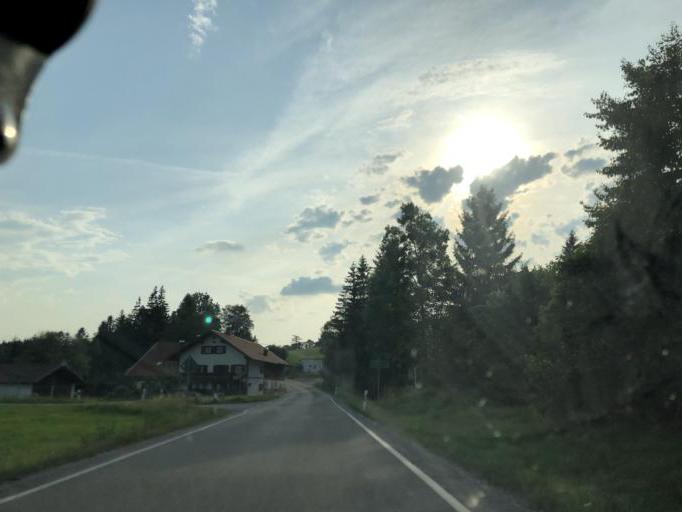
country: DE
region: Bavaria
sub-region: Swabia
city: Unterthingau
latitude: 47.7561
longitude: 10.5367
